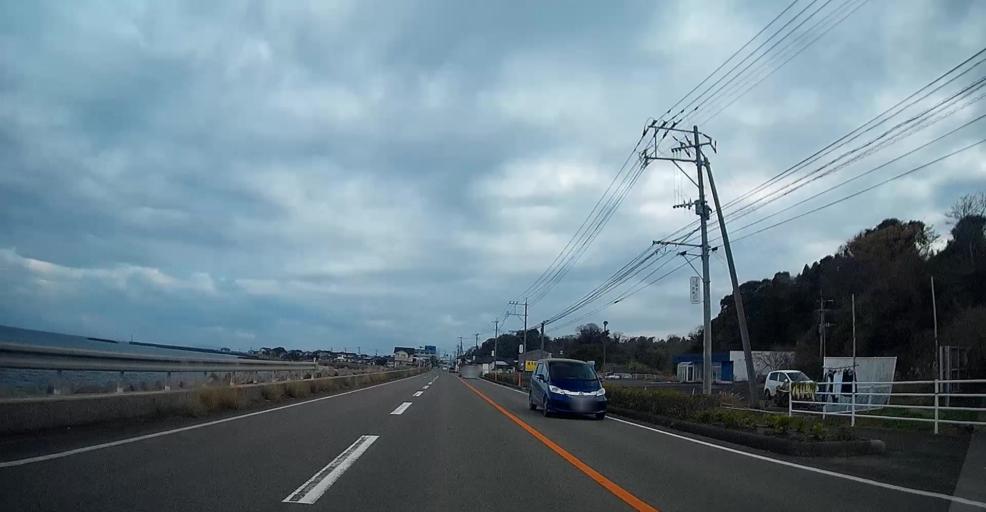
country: JP
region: Kumamoto
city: Hondo
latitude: 32.4692
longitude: 130.2494
